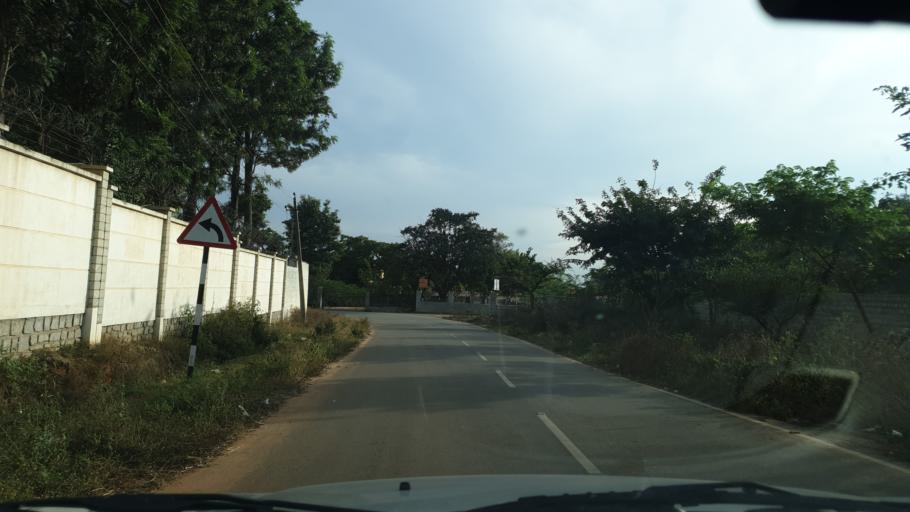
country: IN
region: Karnataka
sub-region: Bangalore Urban
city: Yelahanka
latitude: 13.1928
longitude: 77.6232
